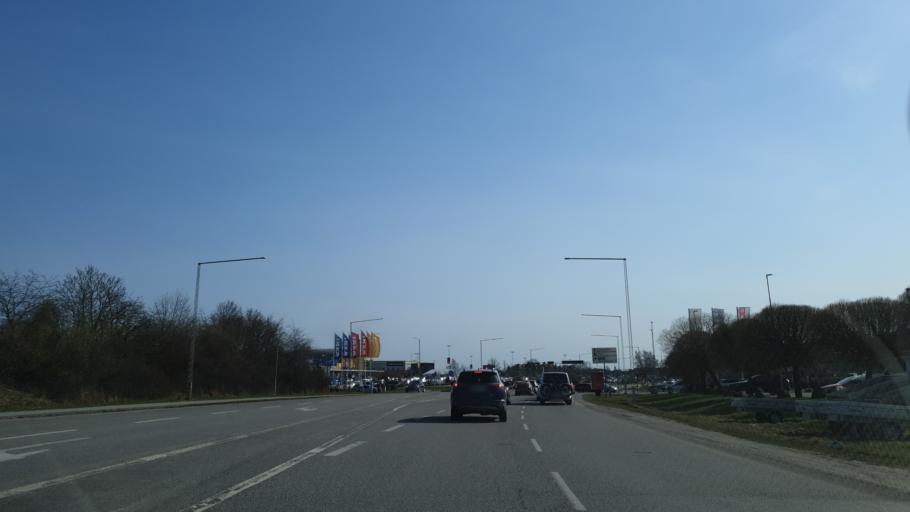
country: SE
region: Stockholm
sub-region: Jarfalla Kommun
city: Jakobsberg
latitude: 59.4236
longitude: 17.8556
